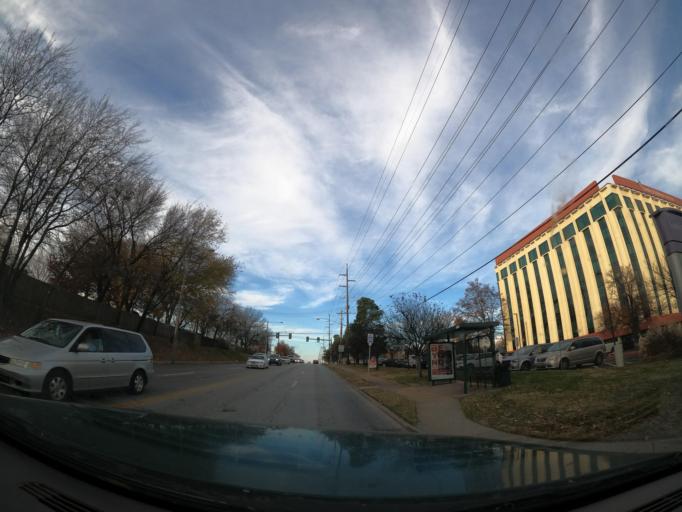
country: US
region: Oklahoma
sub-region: Tulsa County
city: Tulsa
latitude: 36.1280
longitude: -95.9403
